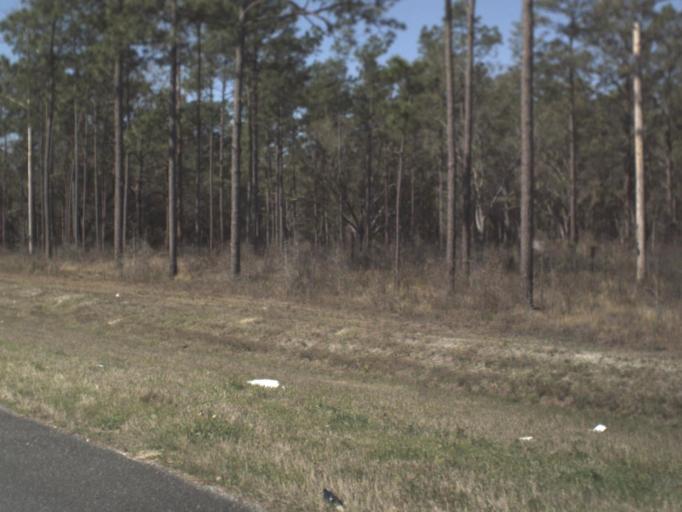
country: US
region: Florida
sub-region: Leon County
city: Woodville
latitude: 30.3477
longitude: -84.3120
